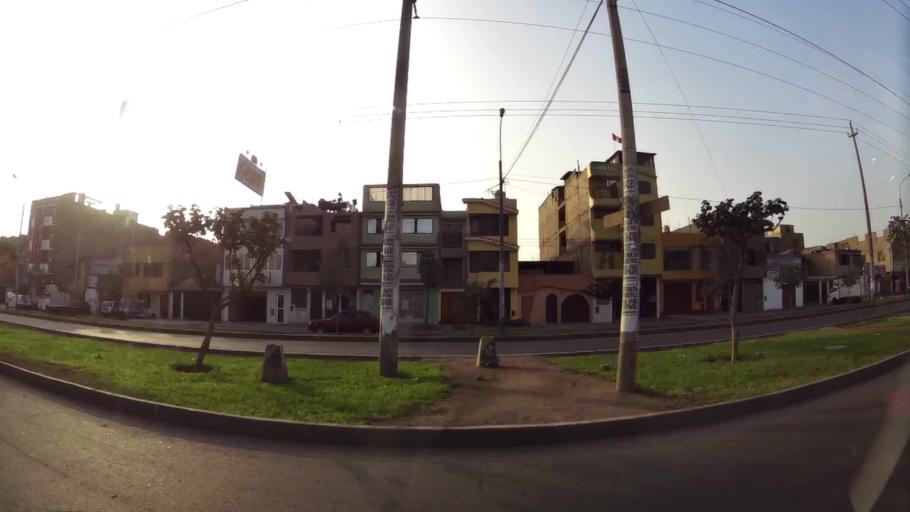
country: PE
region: Lima
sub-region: Lima
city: Independencia
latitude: -11.9472
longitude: -77.0755
